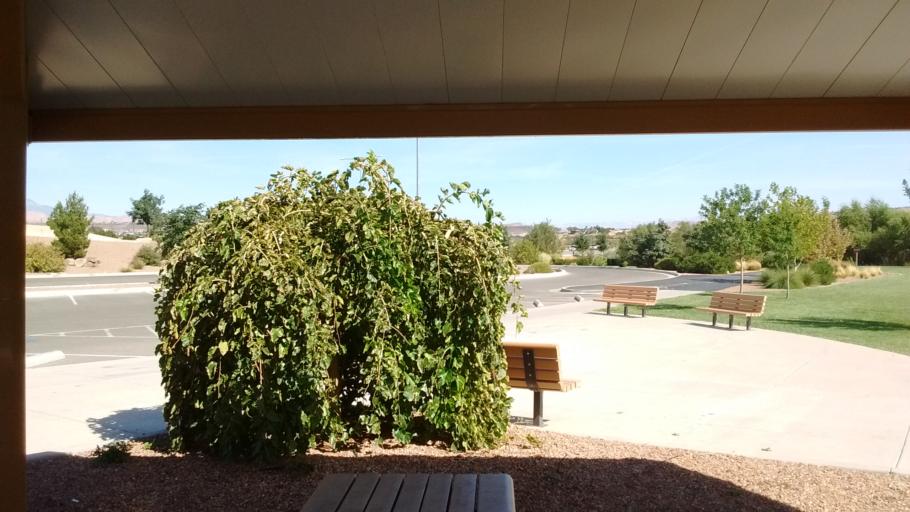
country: US
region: Utah
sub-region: Washington County
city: Saint George
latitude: 37.0746
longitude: -113.5828
